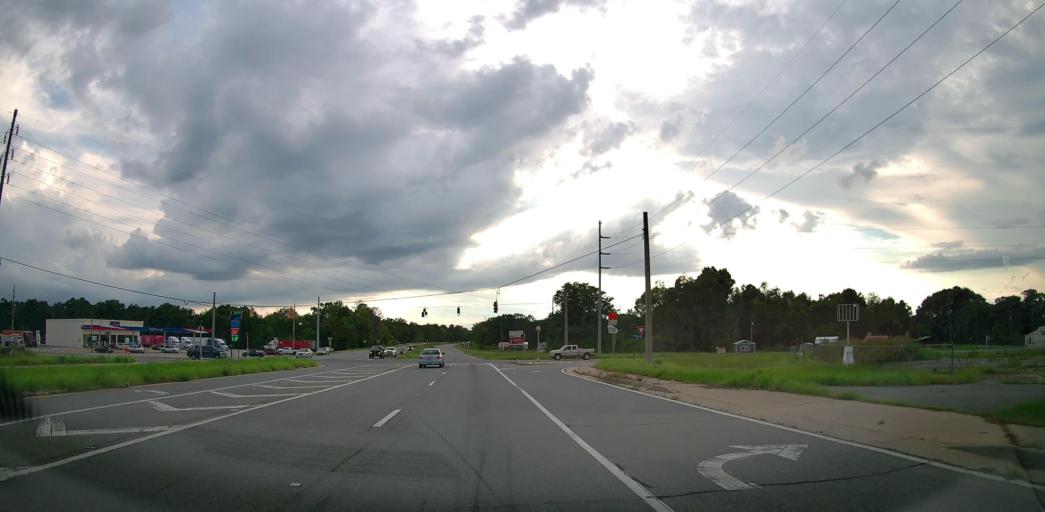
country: US
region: Georgia
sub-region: Pulaski County
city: Hawkinsville
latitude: 32.2823
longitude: -83.4511
